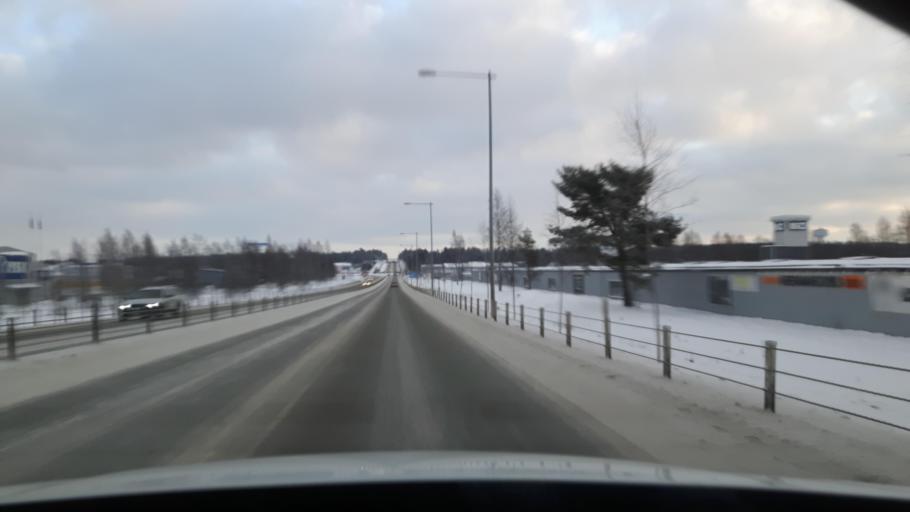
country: SE
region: Vaesterbotten
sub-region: Umea Kommun
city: Ersmark
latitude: 63.8489
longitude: 20.3021
